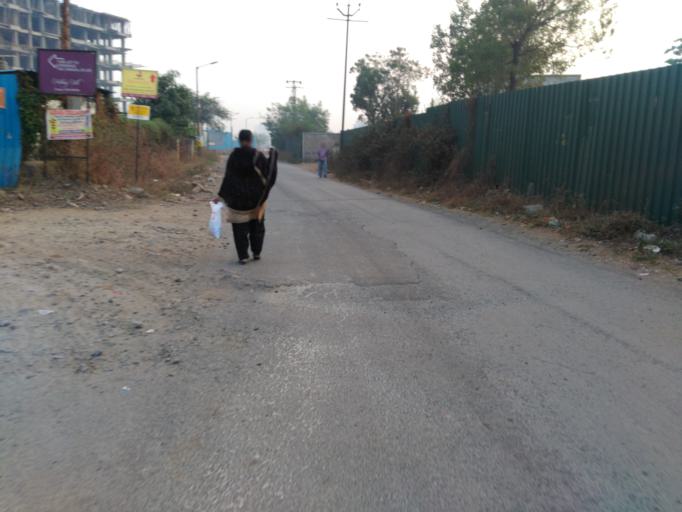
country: IN
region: Maharashtra
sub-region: Pune Division
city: Pune
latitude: 18.4591
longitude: 73.8970
